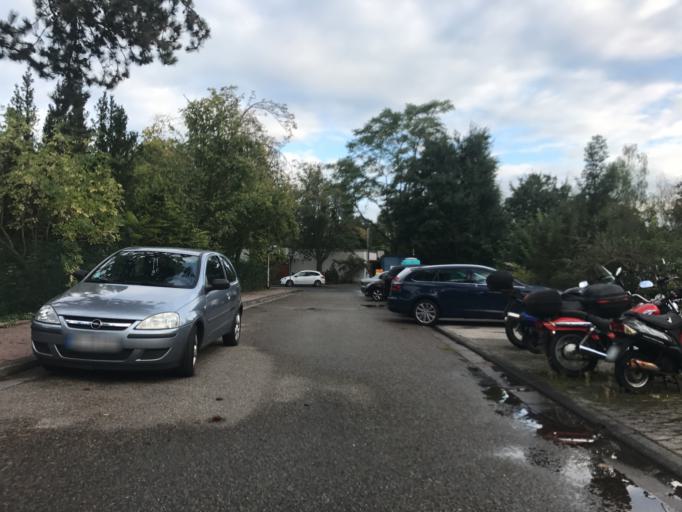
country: DE
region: Rheinland-Pfalz
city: Mainz
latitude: 49.9788
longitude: 8.2530
